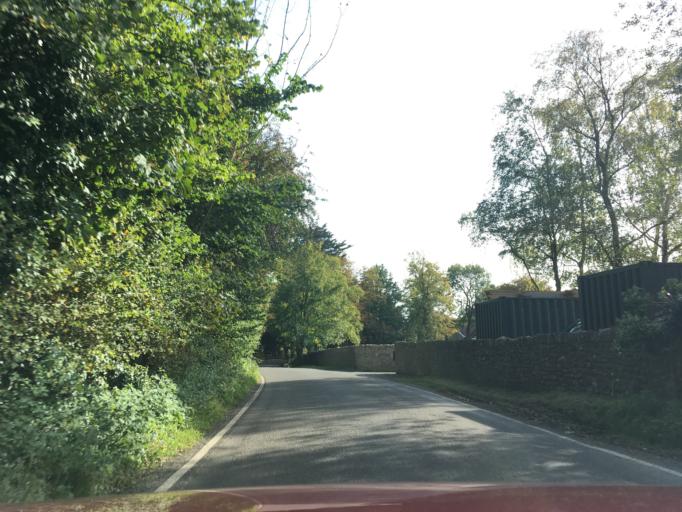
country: GB
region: England
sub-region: South Gloucestershire
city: Chipping Sodbury
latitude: 51.5570
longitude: -2.4029
